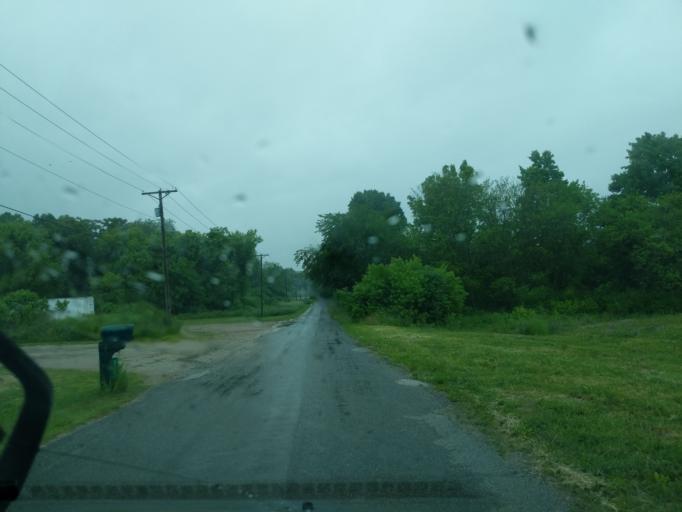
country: US
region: Michigan
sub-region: Berrien County
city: Coloma
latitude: 42.1730
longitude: -86.3080
